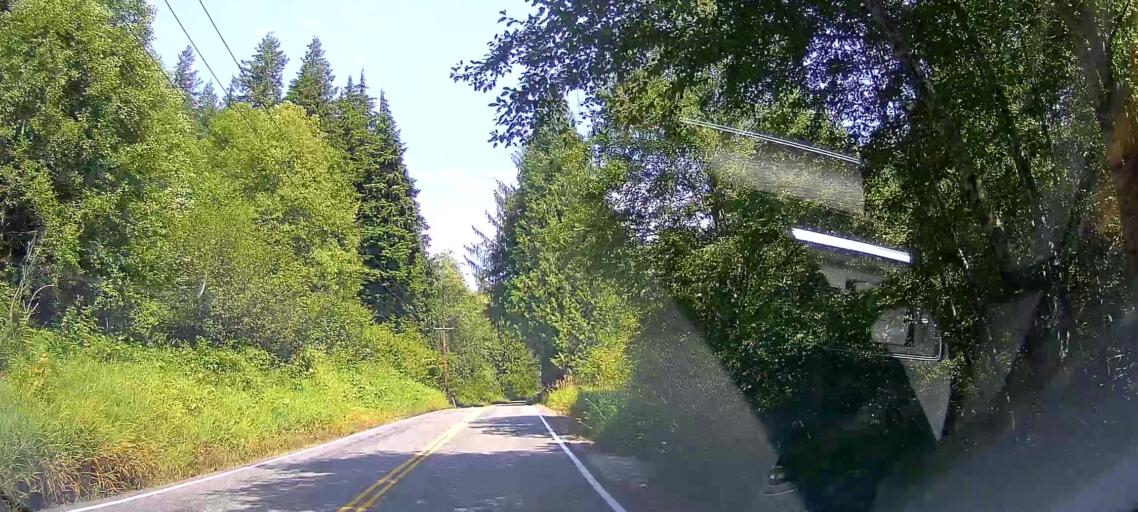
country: US
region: Washington
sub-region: Snohomish County
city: Bryant
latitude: 48.3438
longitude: -122.0811
